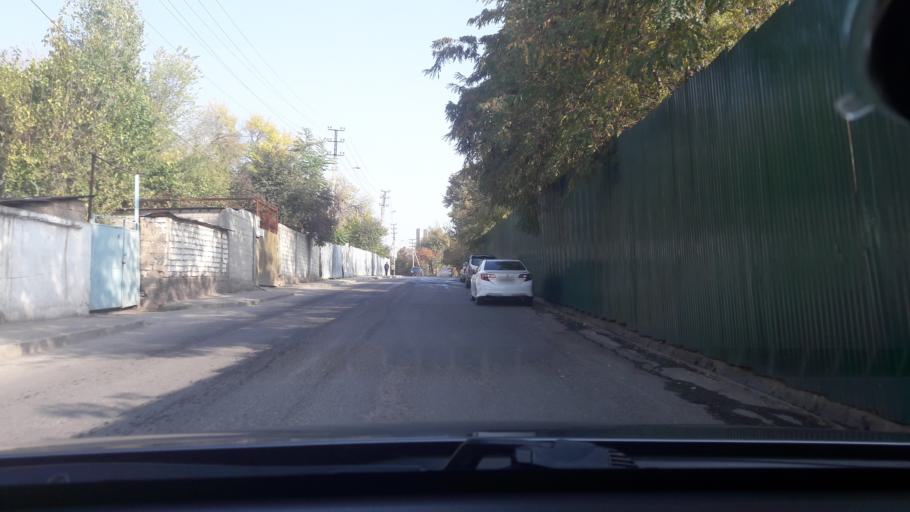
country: TJ
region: Dushanbe
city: Dushanbe
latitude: 38.5629
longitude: 68.7819
